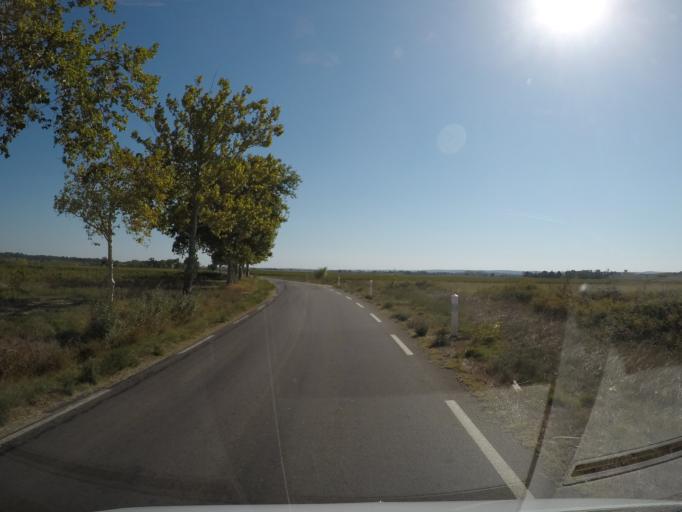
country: FR
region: Languedoc-Roussillon
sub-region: Departement du Gard
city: Moussac
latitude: 43.9823
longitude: 4.2531
